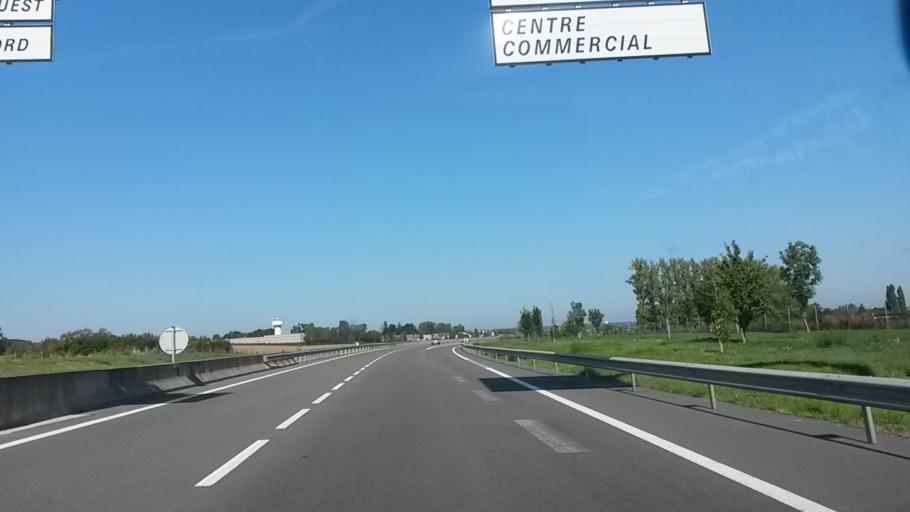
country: FR
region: Nord-Pas-de-Calais
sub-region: Departement du Nord
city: Louvroil
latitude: 50.2415
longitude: 3.9572
